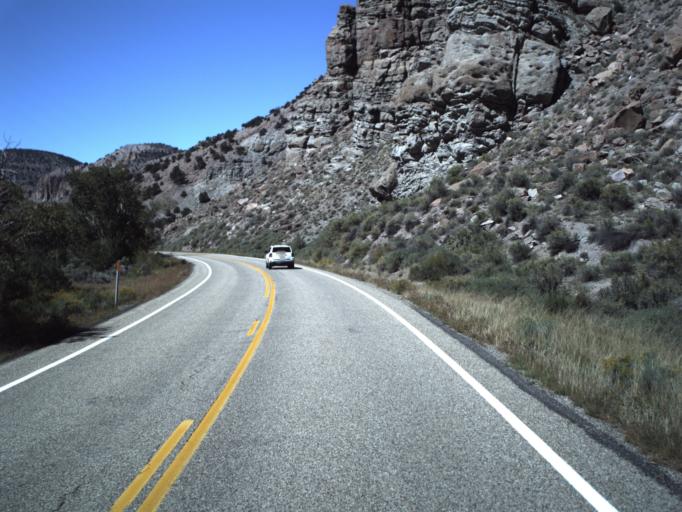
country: US
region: Utah
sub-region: Piute County
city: Junction
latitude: 38.1922
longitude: -112.1045
